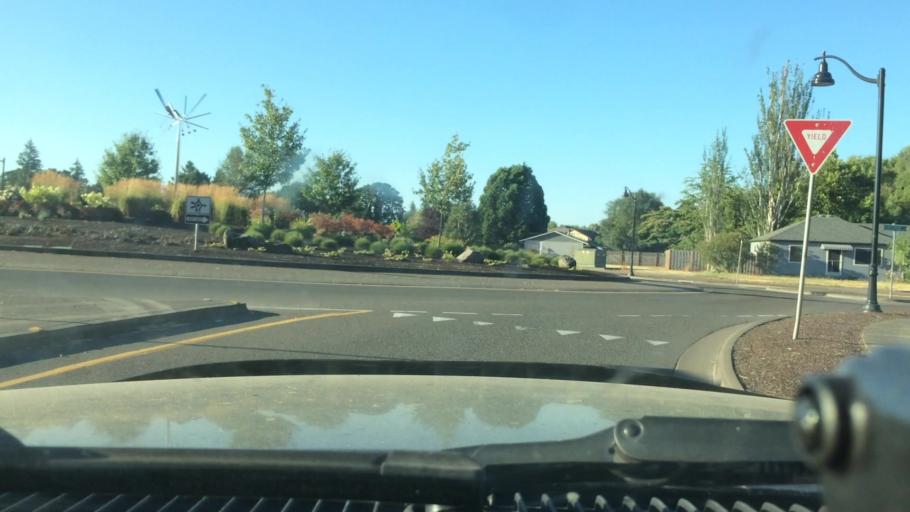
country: US
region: Oregon
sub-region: Yamhill County
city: Newberg
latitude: 45.3157
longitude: -122.9463
